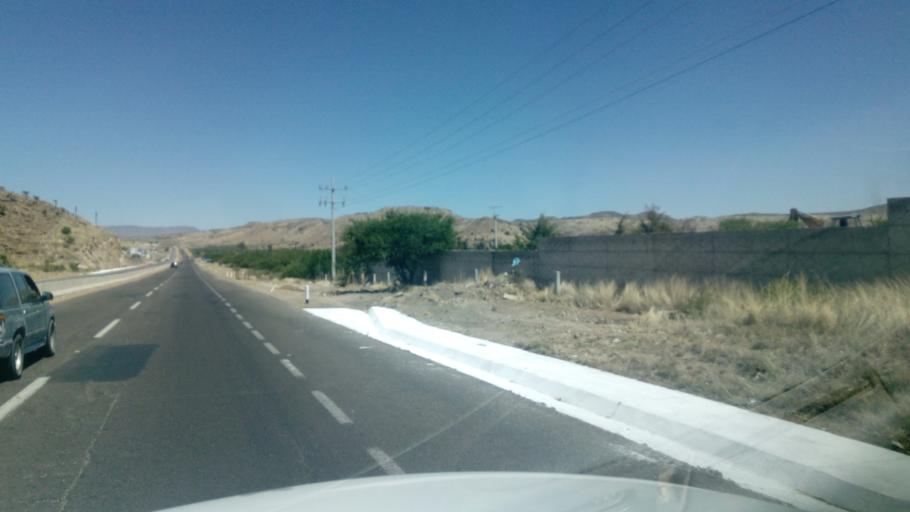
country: MX
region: Durango
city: Victoria de Durango
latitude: 24.0917
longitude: -104.6829
